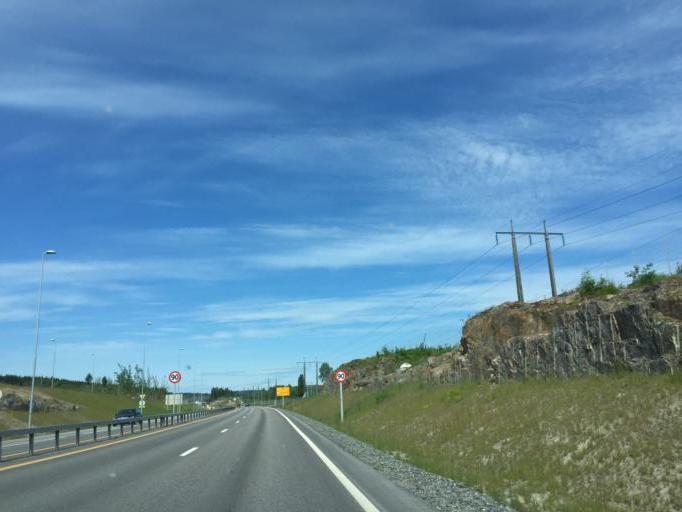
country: NO
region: Hedmark
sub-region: Kongsvinger
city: Kongsvinger
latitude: 60.1958
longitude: 11.9747
